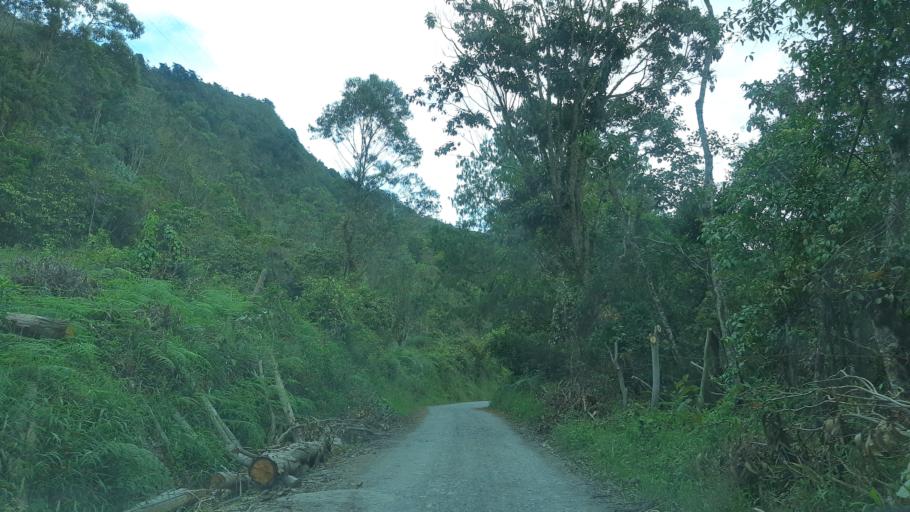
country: CO
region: Boyaca
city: Garagoa
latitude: 4.9863
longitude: -73.3247
